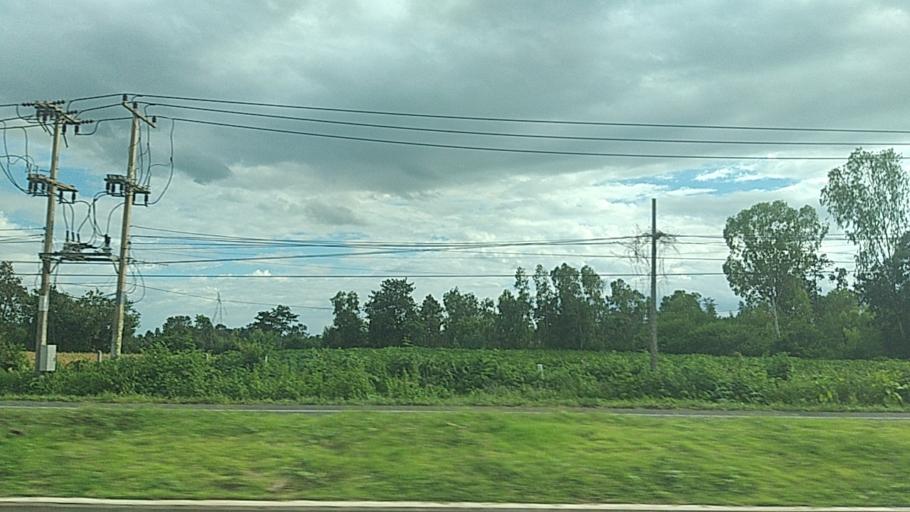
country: TH
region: Surin
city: Prasat
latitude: 14.6032
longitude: 103.4298
